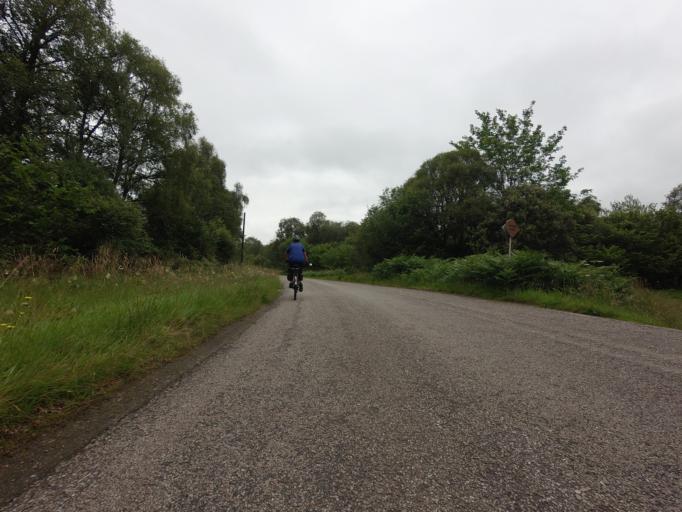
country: GB
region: Scotland
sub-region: Highland
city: Evanton
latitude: 57.9700
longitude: -4.4126
